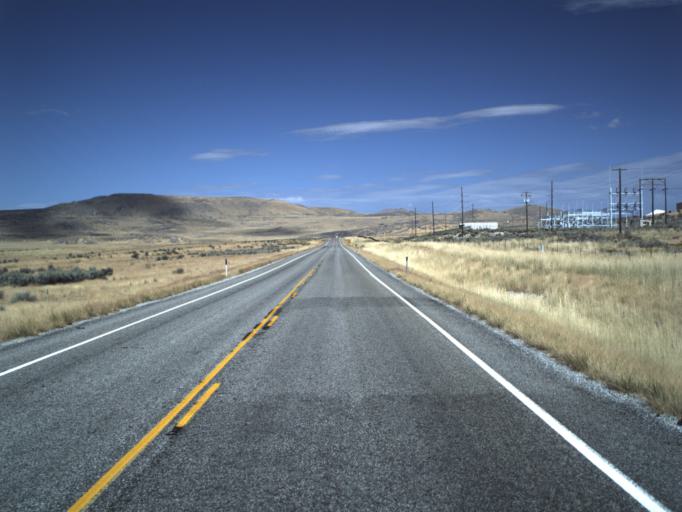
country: US
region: Utah
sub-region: Box Elder County
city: Tremonton
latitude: 41.6429
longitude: -112.4295
